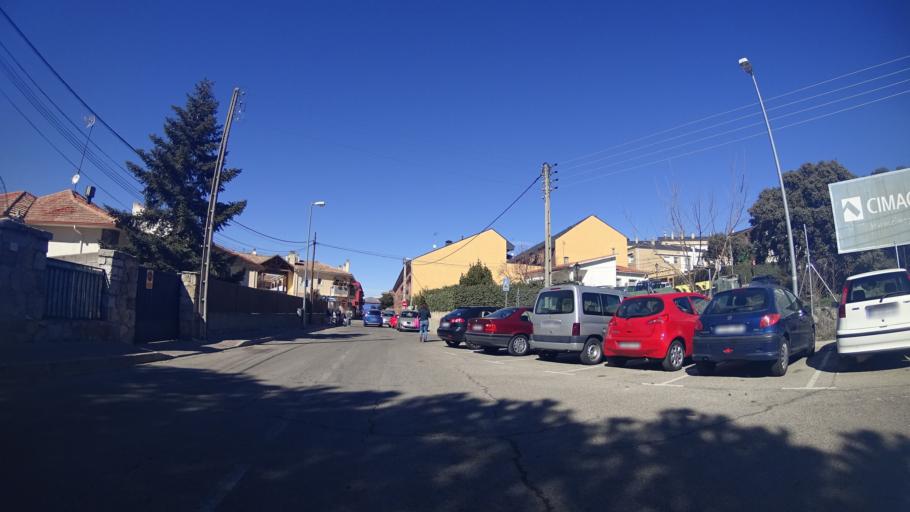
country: ES
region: Madrid
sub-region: Provincia de Madrid
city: Colmenarejo
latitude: 40.5585
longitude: -4.0149
